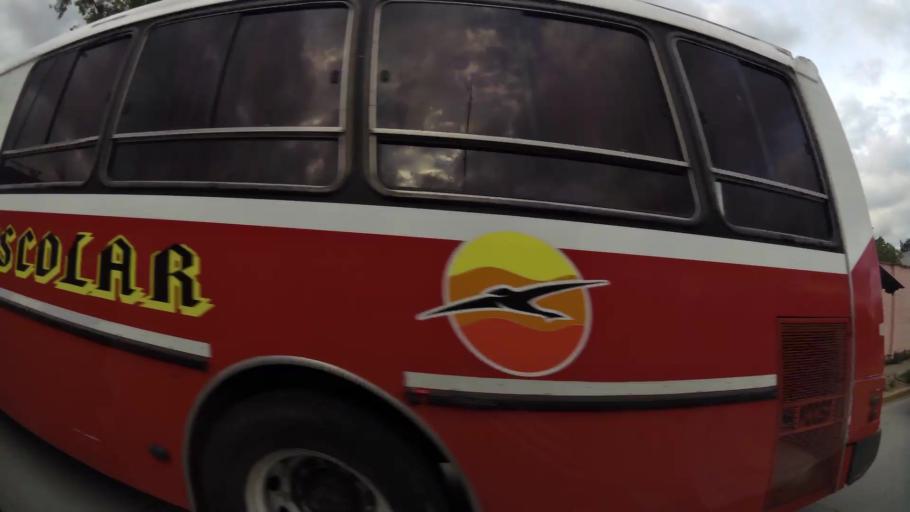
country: AR
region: Buenos Aires
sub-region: Partido de Quilmes
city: Quilmes
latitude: -34.7448
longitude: -58.2287
